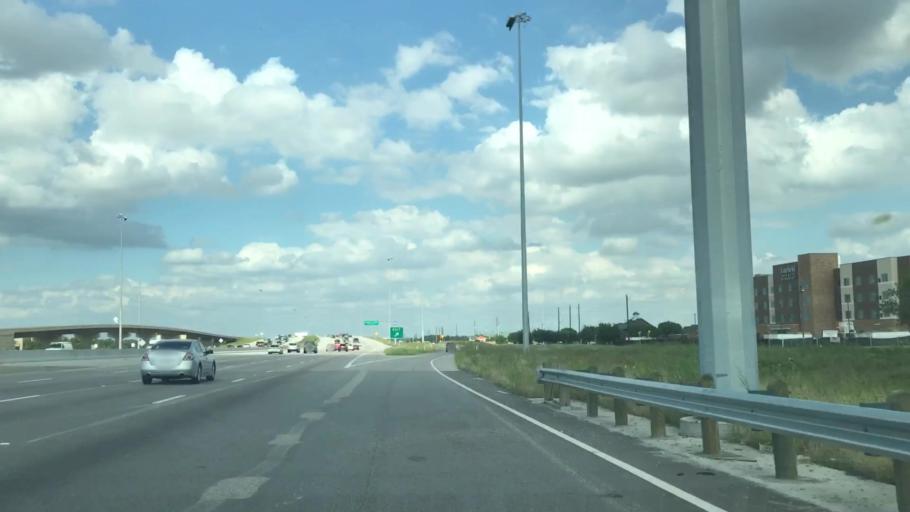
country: US
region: Texas
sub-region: Dallas County
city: Coppell
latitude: 32.9682
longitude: -97.0328
